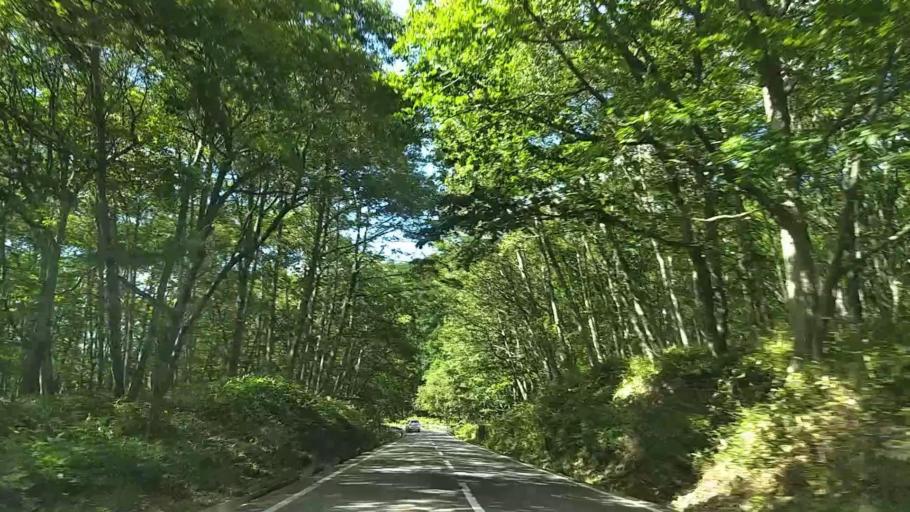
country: JP
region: Nagano
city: Chino
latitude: 36.0973
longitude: 138.2745
